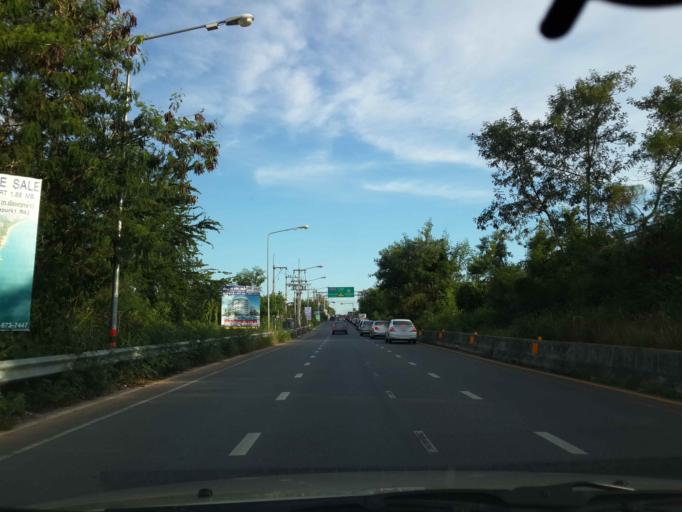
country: TH
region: Chon Buri
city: Phatthaya
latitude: 12.9022
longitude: 100.9009
